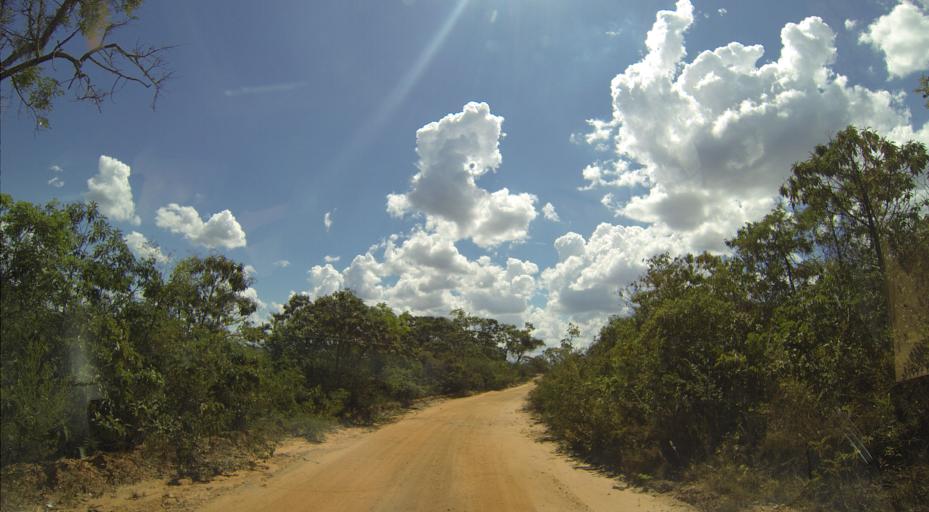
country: BR
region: Minas Gerais
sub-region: Serro
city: Serro
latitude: -18.4847
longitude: -43.4669
